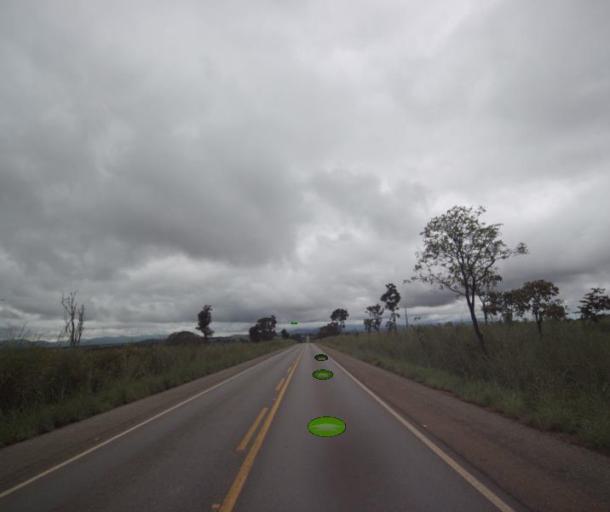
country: BR
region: Goias
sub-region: Barro Alto
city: Barro Alto
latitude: -14.7992
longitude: -49.0493
